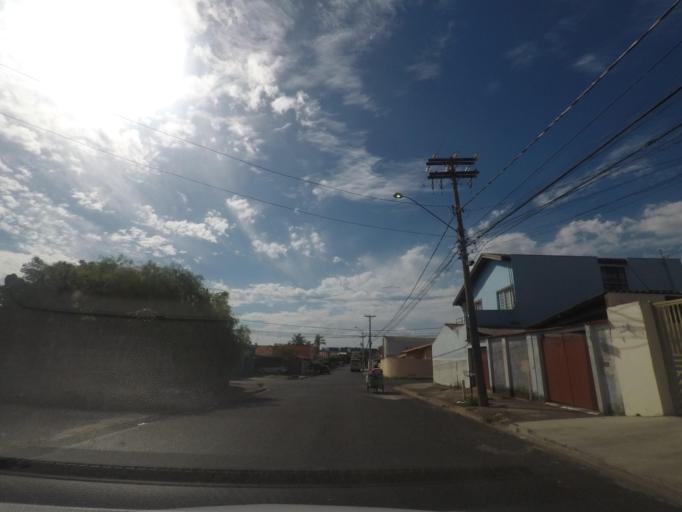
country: BR
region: Sao Paulo
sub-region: Sumare
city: Sumare
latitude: -22.8064
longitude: -47.2666
